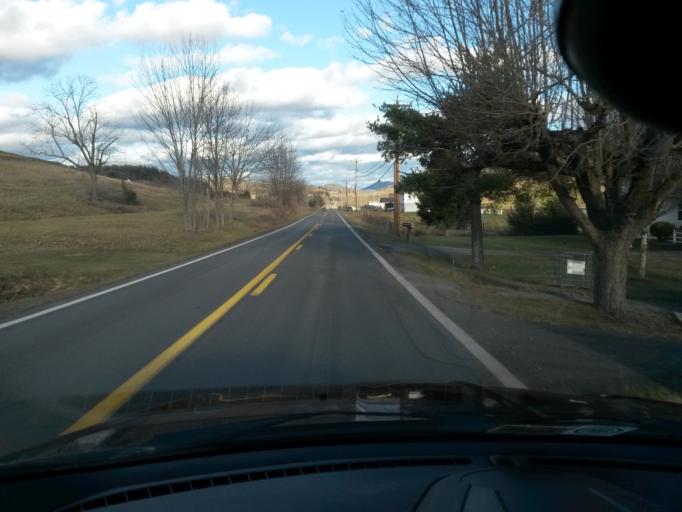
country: US
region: Virginia
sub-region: Giles County
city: Pearisburg
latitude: 37.4144
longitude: -80.7485
